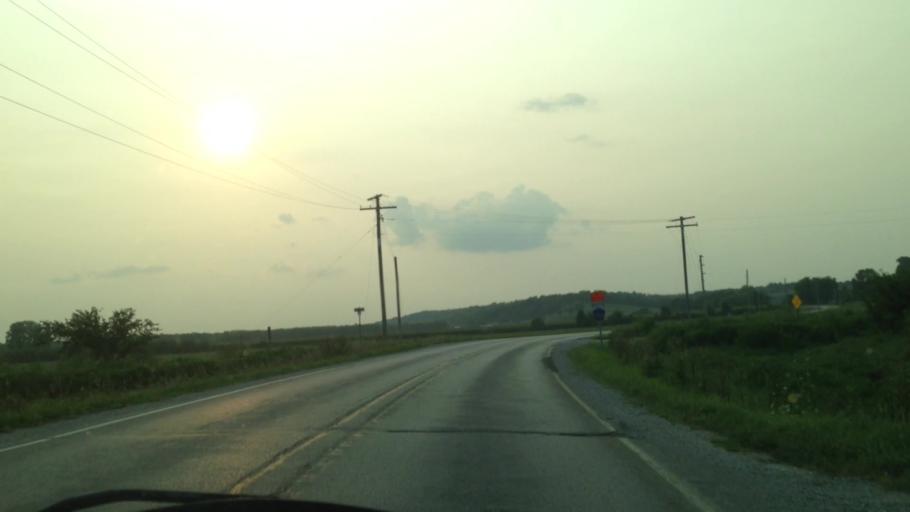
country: US
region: Iowa
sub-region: Iowa County
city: Marengo
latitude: 41.8239
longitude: -92.0685
